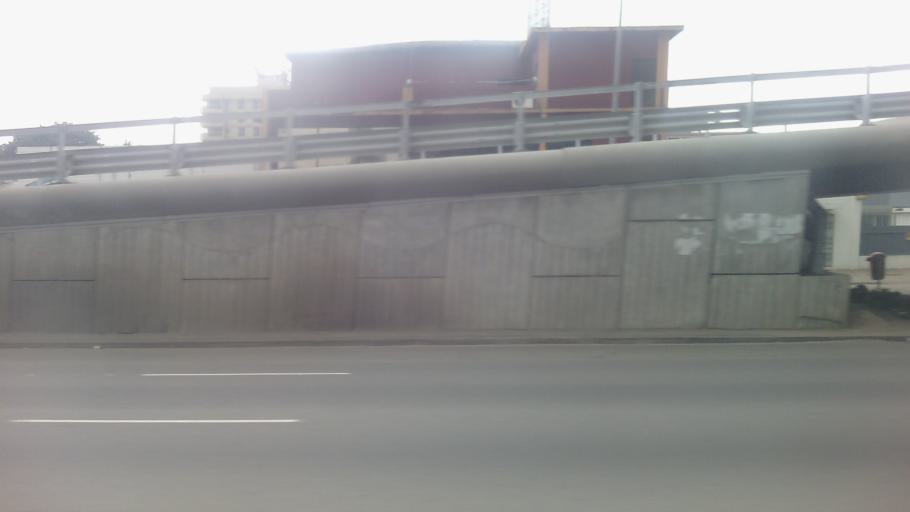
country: CI
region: Lagunes
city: Abidjan
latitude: 5.2955
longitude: -3.9803
